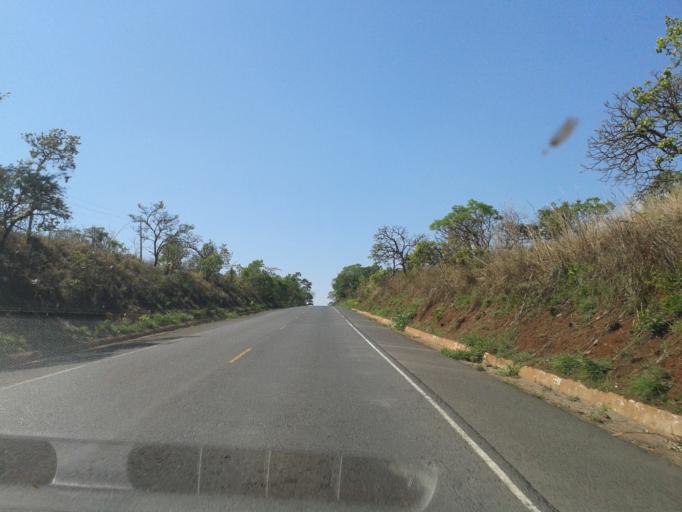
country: BR
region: Minas Gerais
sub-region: Uberlandia
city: Uberlandia
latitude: -19.0918
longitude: -47.9990
